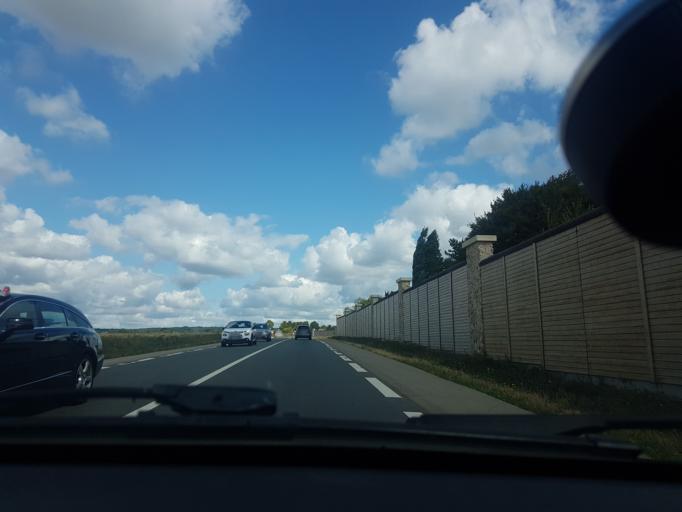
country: FR
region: Ile-de-France
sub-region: Departement des Yvelines
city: Saint-Nom-la-Breteche
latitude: 48.8484
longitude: 2.0169
